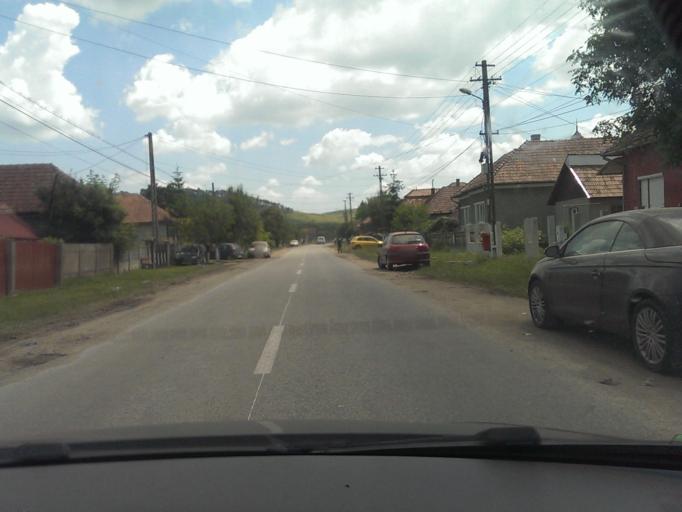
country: RO
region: Cluj
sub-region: Comuna Bontida
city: Rascruci
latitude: 46.9232
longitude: 23.8035
